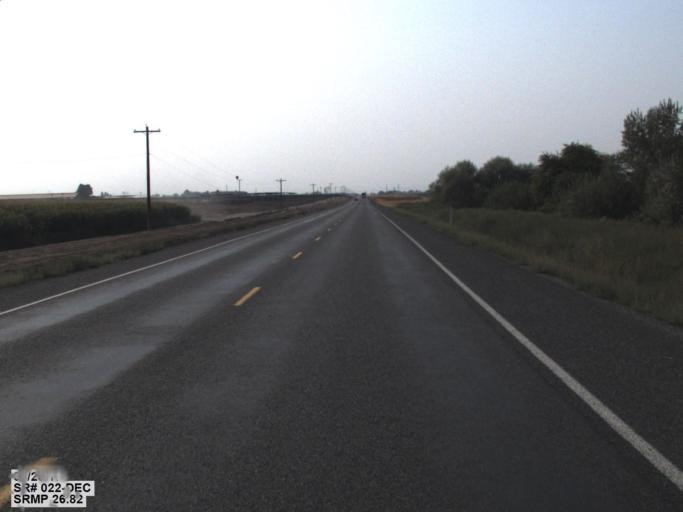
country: US
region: Washington
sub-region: Yakima County
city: Grandview
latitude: 46.1938
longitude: -119.9268
